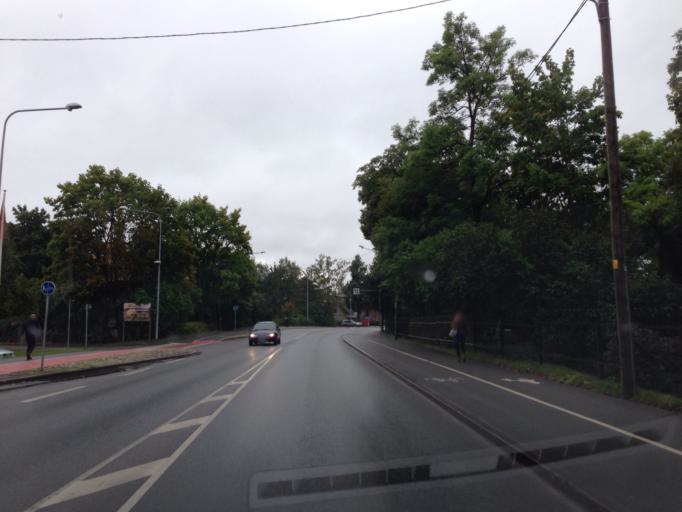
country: EE
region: Tartu
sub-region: Tartu linn
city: Tartu
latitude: 58.3584
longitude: 26.7218
